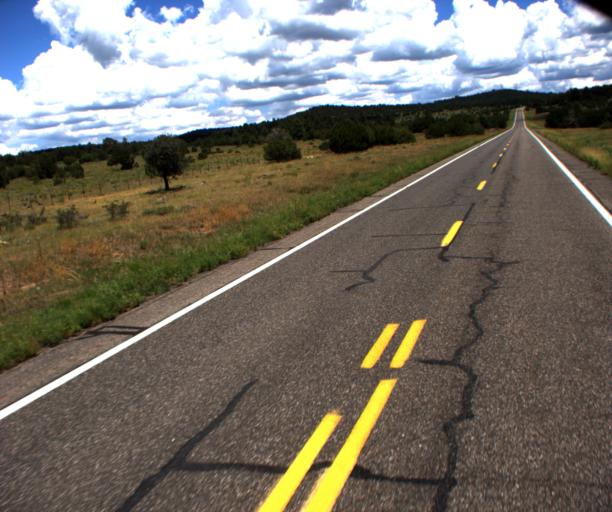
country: US
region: Arizona
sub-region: Gila County
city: Pine
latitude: 34.5063
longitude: -111.5686
